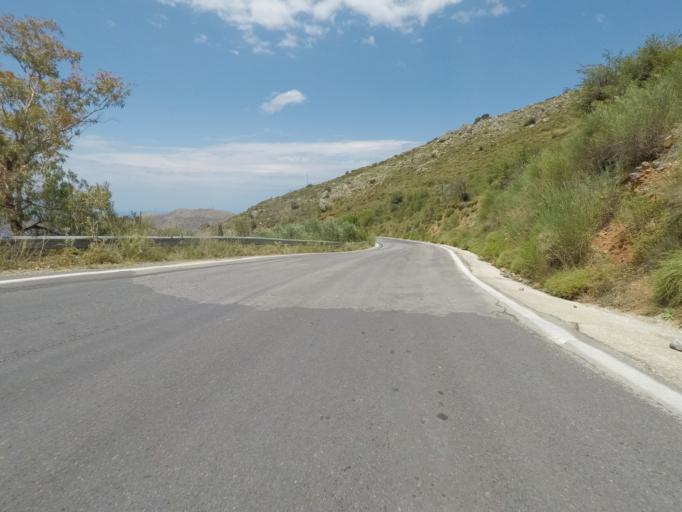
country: GR
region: Crete
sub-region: Nomos Irakleiou
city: Mokhos
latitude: 35.2153
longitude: 25.4591
